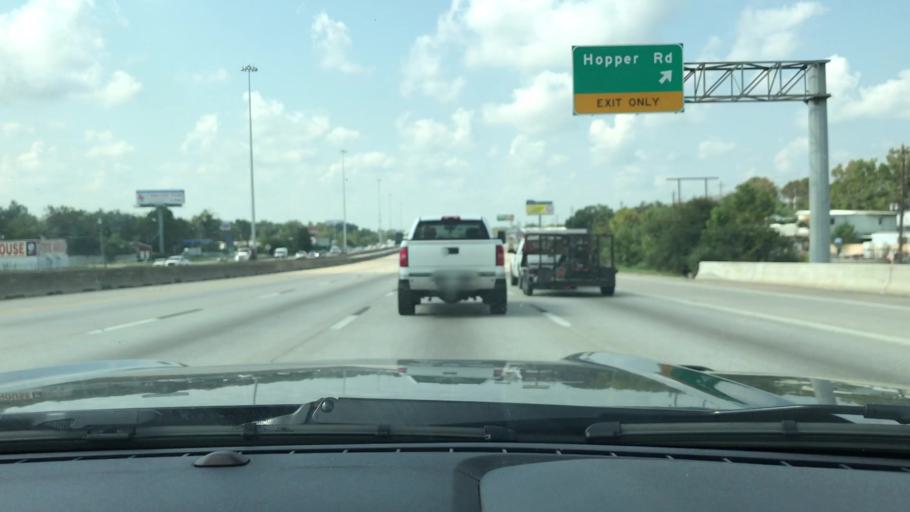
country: US
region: Texas
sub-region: Harris County
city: Aldine
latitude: 29.8889
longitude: -95.3195
